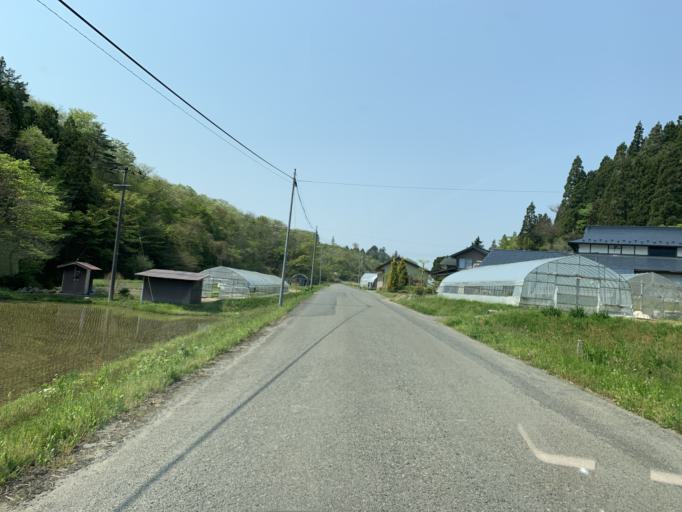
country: JP
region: Iwate
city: Ichinoseki
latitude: 38.8937
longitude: 141.0763
